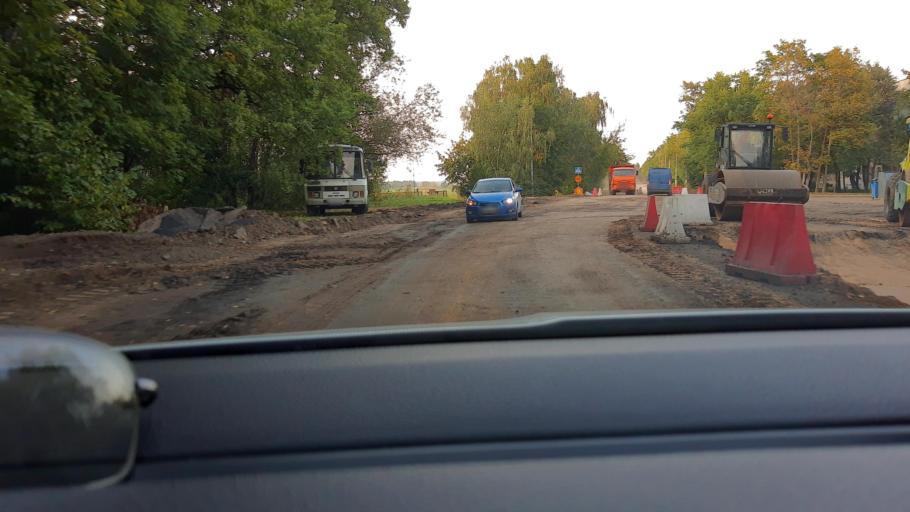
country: RU
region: Moskovskaya
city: Troitsk
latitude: 55.3150
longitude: 37.1745
